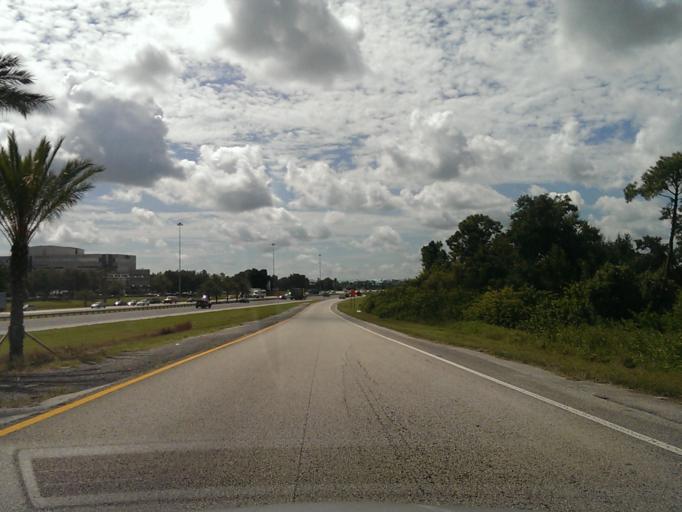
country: US
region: Florida
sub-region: Orange County
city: Williamsburg
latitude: 28.4187
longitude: -81.4750
